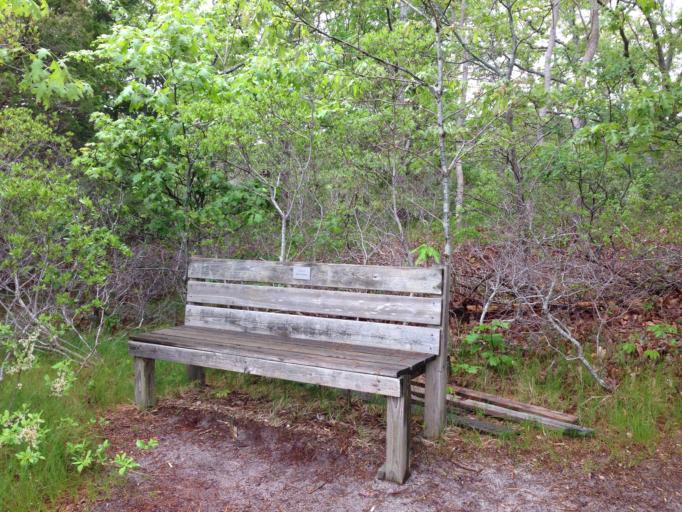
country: US
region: Massachusetts
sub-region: Barnstable County
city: North Eastham
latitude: 41.8812
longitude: -69.9980
